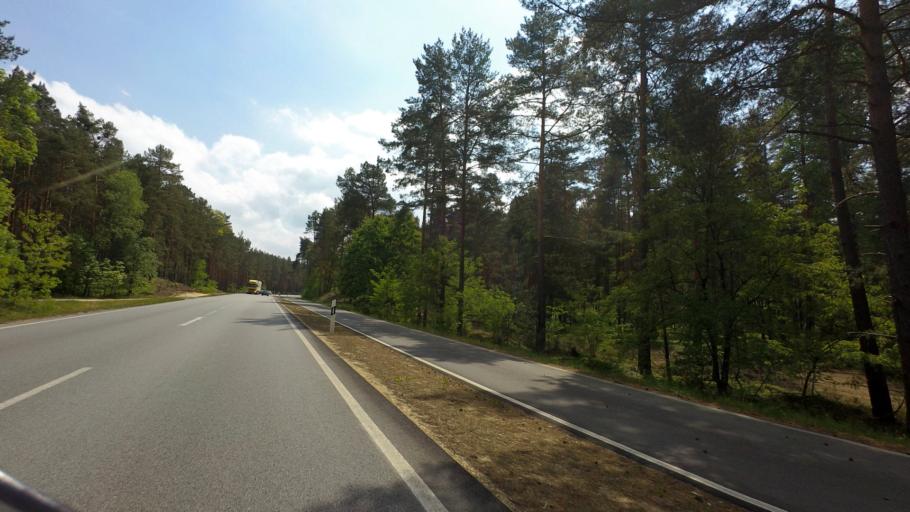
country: DE
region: Saxony
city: Rietschen
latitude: 51.4240
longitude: 14.7887
